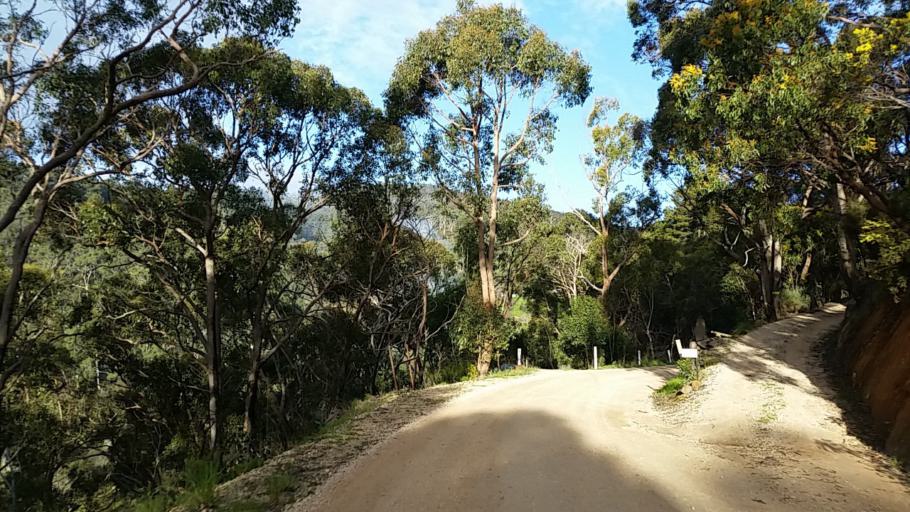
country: AU
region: South Australia
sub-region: Adelaide Hills
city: Adelaide Hills
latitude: -34.9280
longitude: 138.7785
